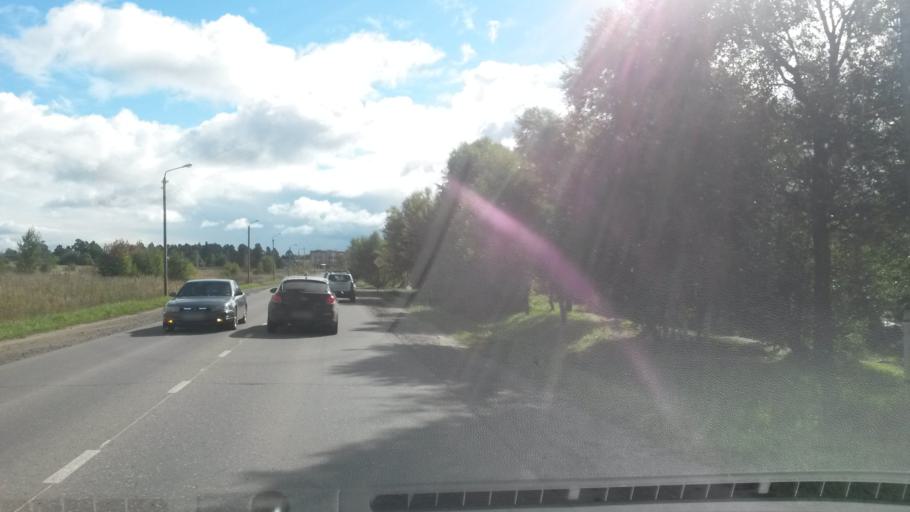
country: RU
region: Ivanovo
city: Zavolzhsk
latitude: 57.4983
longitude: 42.1265
